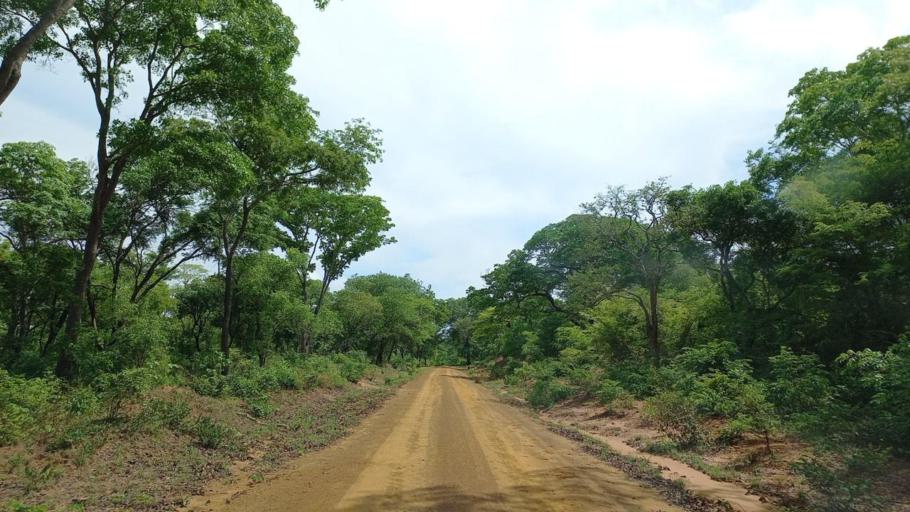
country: ZM
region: North-Western
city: Kabompo
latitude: -13.5422
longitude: 24.0999
